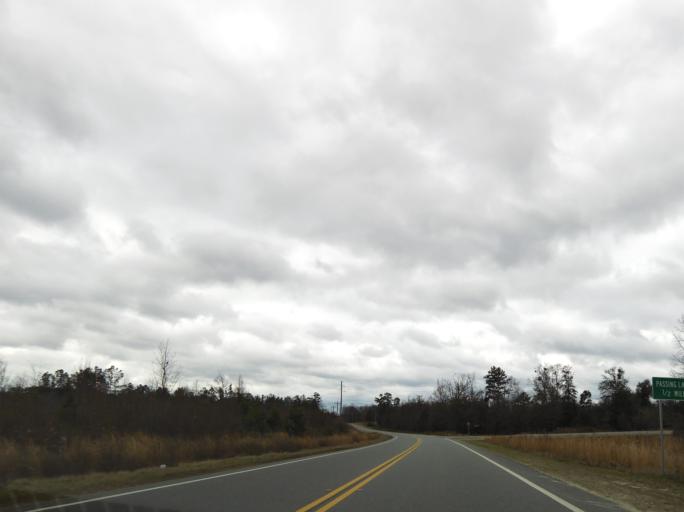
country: US
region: Georgia
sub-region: Twiggs County
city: Jeffersonville
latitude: 32.6094
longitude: -83.3733
